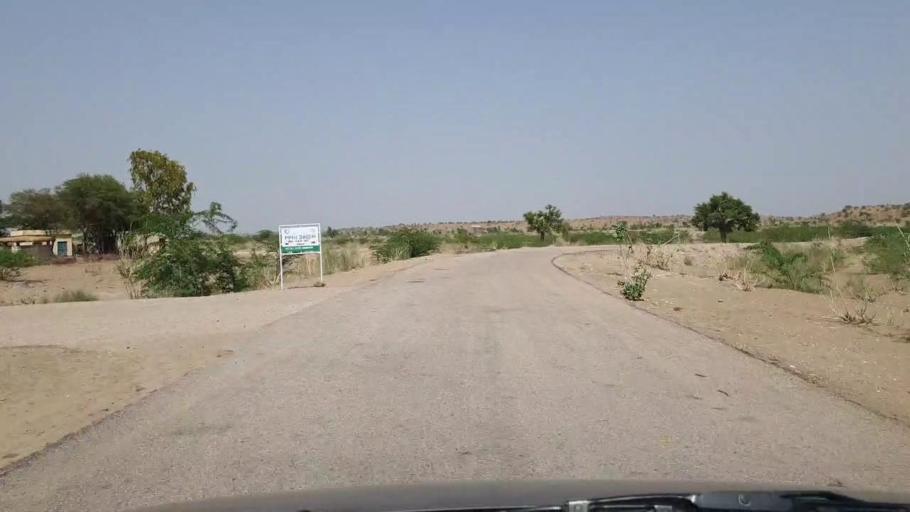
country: PK
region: Sindh
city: Chor
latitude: 25.4739
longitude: 70.5124
